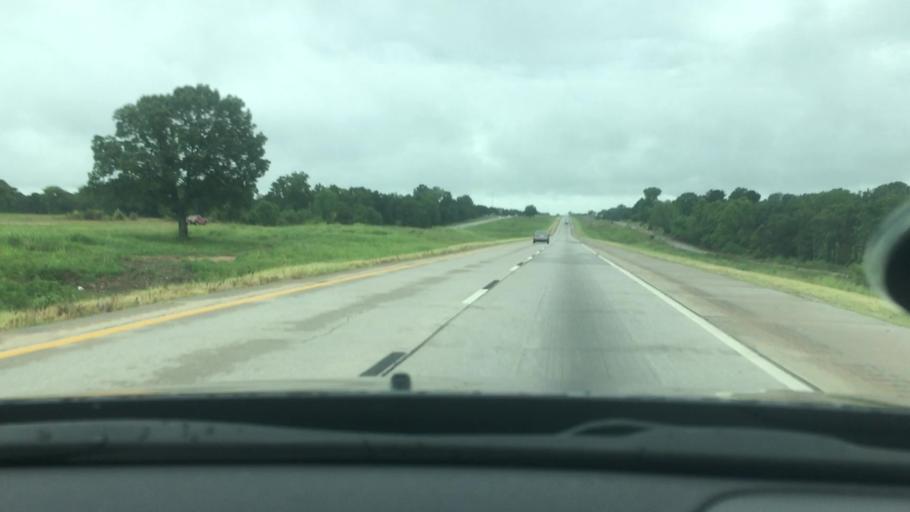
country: US
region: Oklahoma
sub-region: Atoka County
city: Atoka
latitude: 34.2142
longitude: -96.2321
